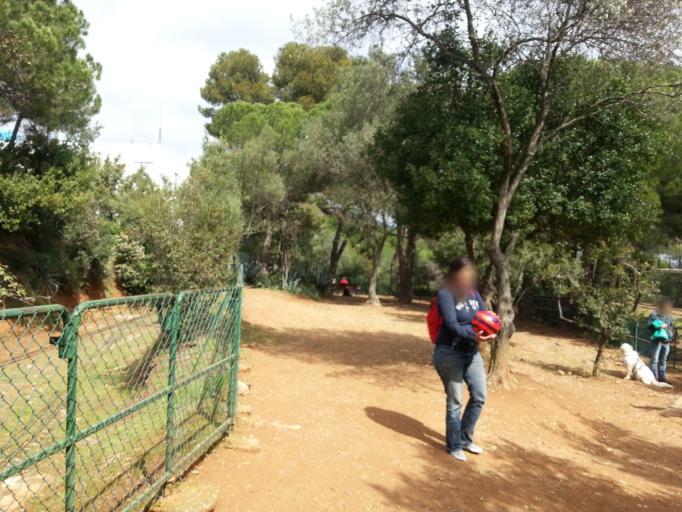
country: ES
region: Catalonia
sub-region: Provincia de Barcelona
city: les Corts
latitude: 41.4007
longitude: 2.1082
